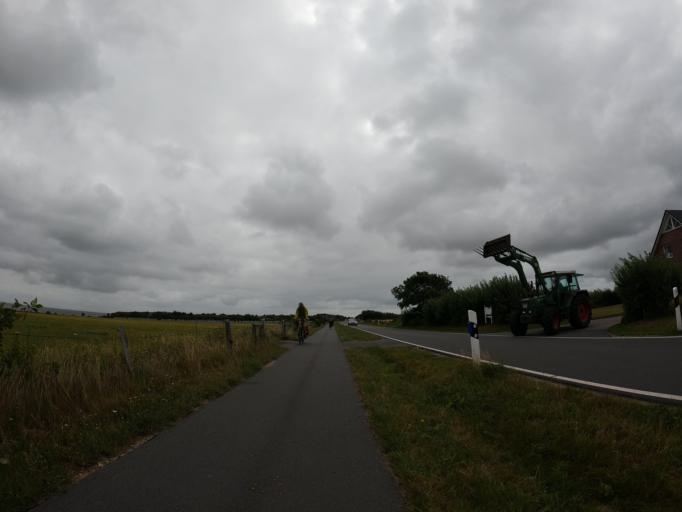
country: DE
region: Schleswig-Holstein
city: Tinnum
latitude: 54.9441
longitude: 8.3477
